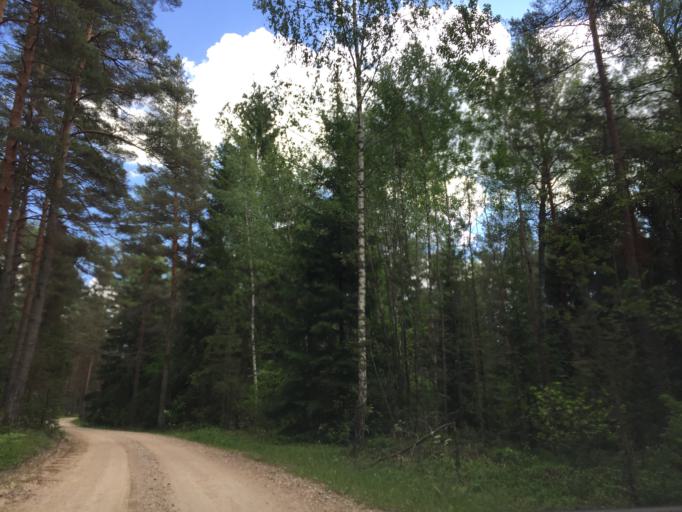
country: LV
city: Tireli
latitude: 56.8641
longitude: 23.6448
